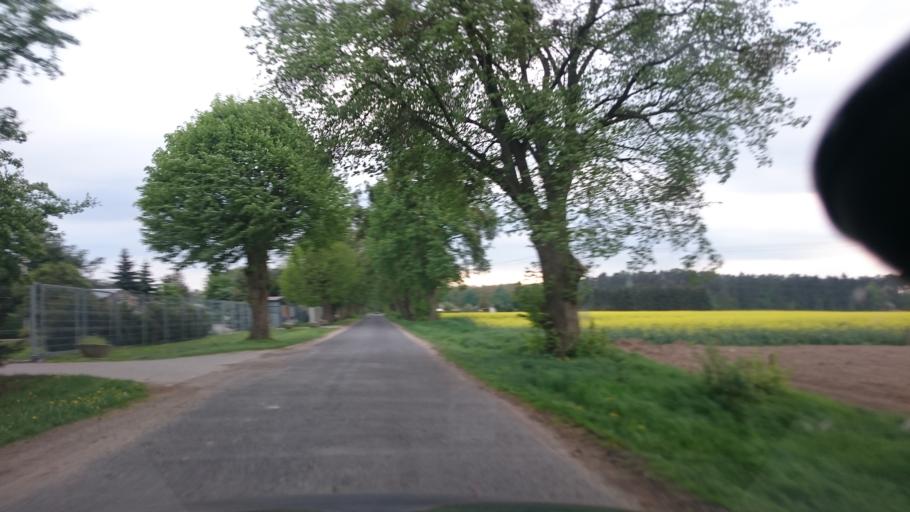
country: PL
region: Kujawsko-Pomorskie
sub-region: Grudziadz
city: Grudziadz
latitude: 53.4491
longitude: 18.8207
